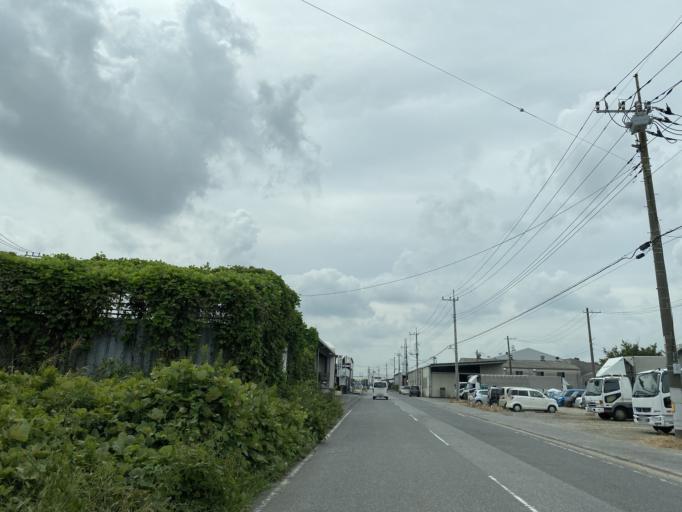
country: JP
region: Ibaraki
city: Mitsukaido
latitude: 36.0296
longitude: 140.0481
